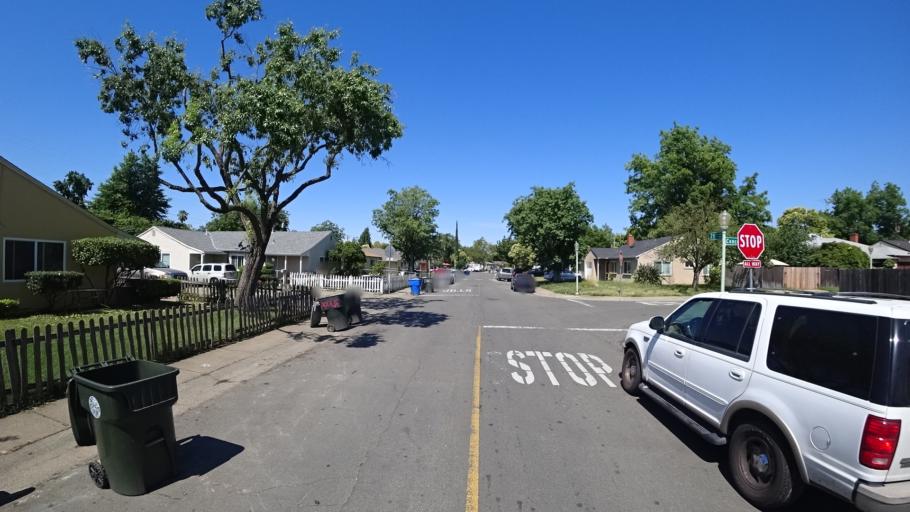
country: US
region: California
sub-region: Sacramento County
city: Florin
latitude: 38.5291
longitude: -121.4175
